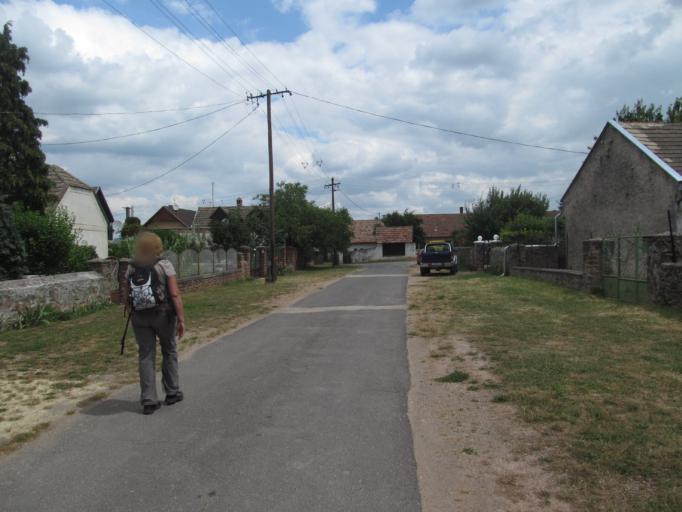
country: HU
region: Veszprem
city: Revfueloep
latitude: 46.8518
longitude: 17.6058
